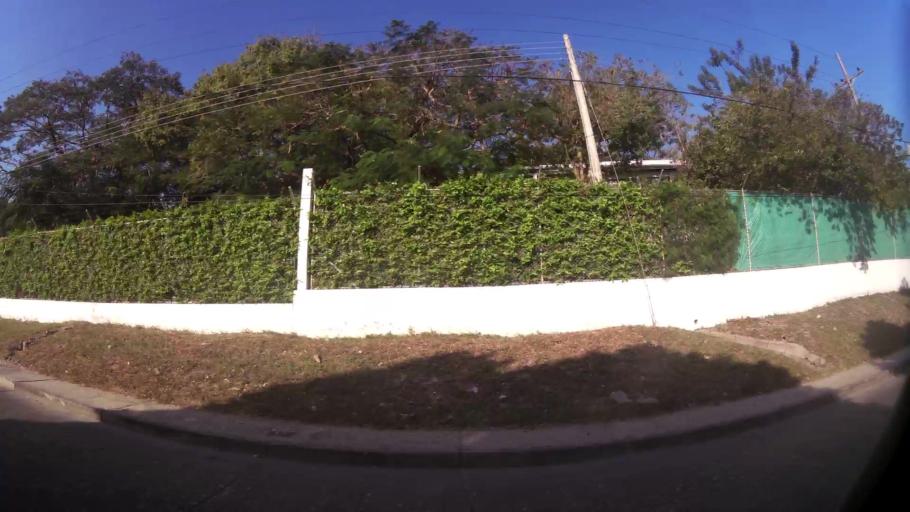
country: CO
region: Bolivar
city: Cartagena
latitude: 10.4046
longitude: -75.5022
